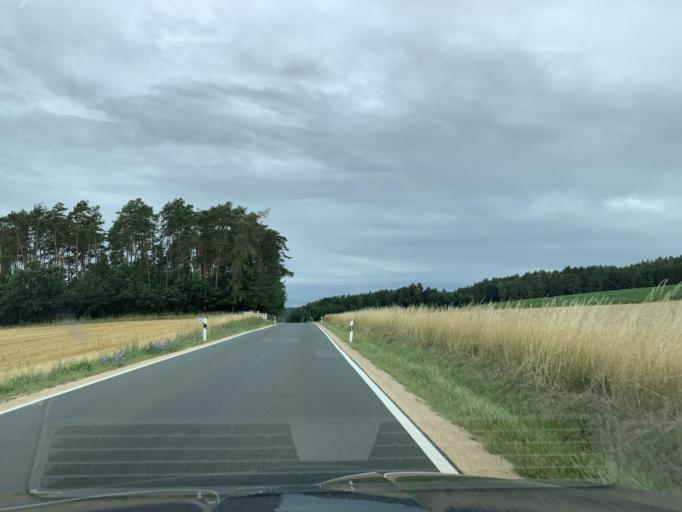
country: DE
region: Bavaria
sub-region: Upper Palatinate
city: Pettendorf
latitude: 49.3612
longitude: 12.3693
